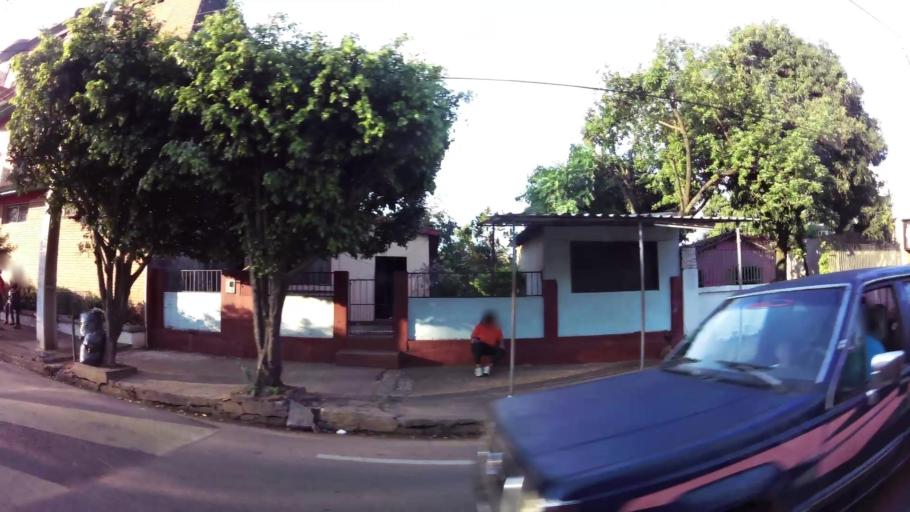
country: PY
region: Central
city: San Lorenzo
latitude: -25.3608
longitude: -57.5059
